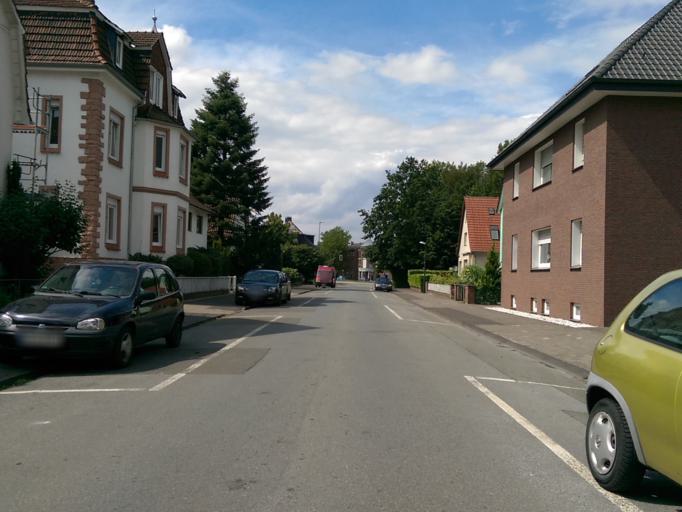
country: DE
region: North Rhine-Westphalia
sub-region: Regierungsbezirk Detmold
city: Guetersloh
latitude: 51.9141
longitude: 8.3841
